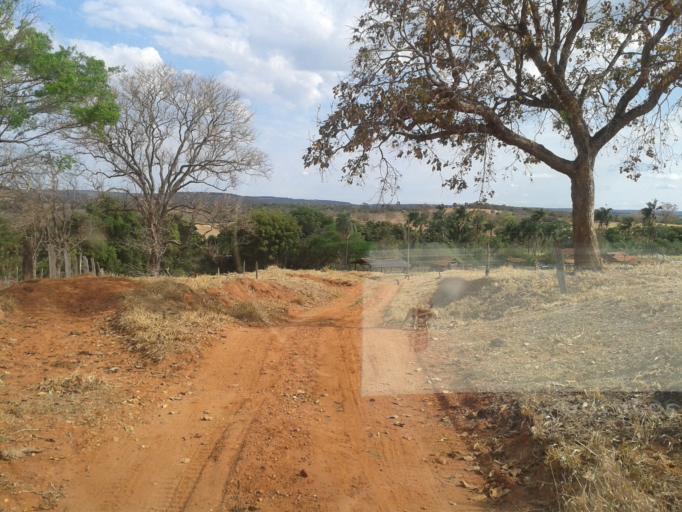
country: BR
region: Minas Gerais
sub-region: Ituiutaba
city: Ituiutaba
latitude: -19.0263
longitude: -49.2106
